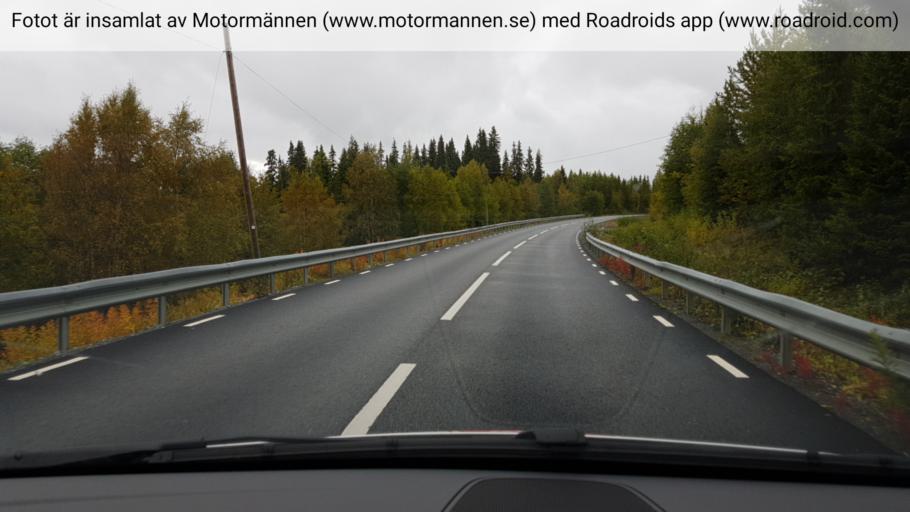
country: SE
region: Jaemtland
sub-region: Are Kommun
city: Are
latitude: 63.4059
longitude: 12.8045
